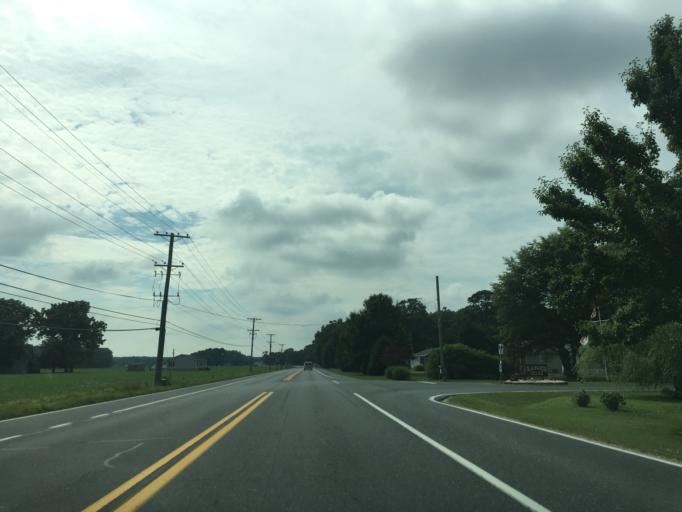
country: US
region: Delaware
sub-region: Sussex County
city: Long Neck
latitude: 38.5558
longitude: -75.1585
